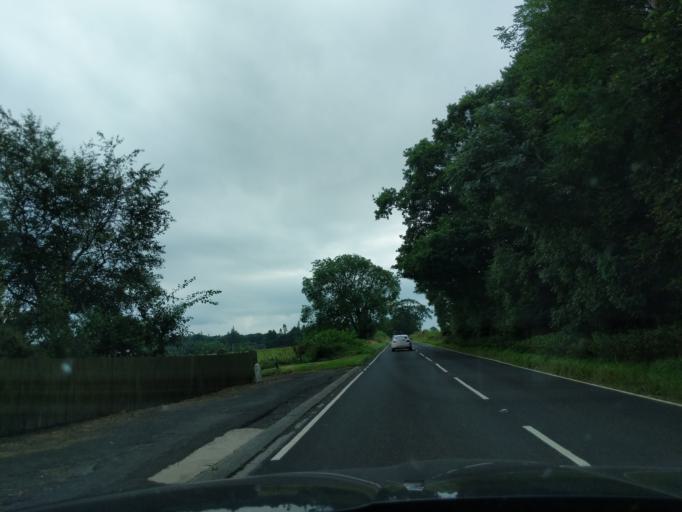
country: GB
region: England
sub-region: Northumberland
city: Whittingham
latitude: 55.4670
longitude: -1.9168
